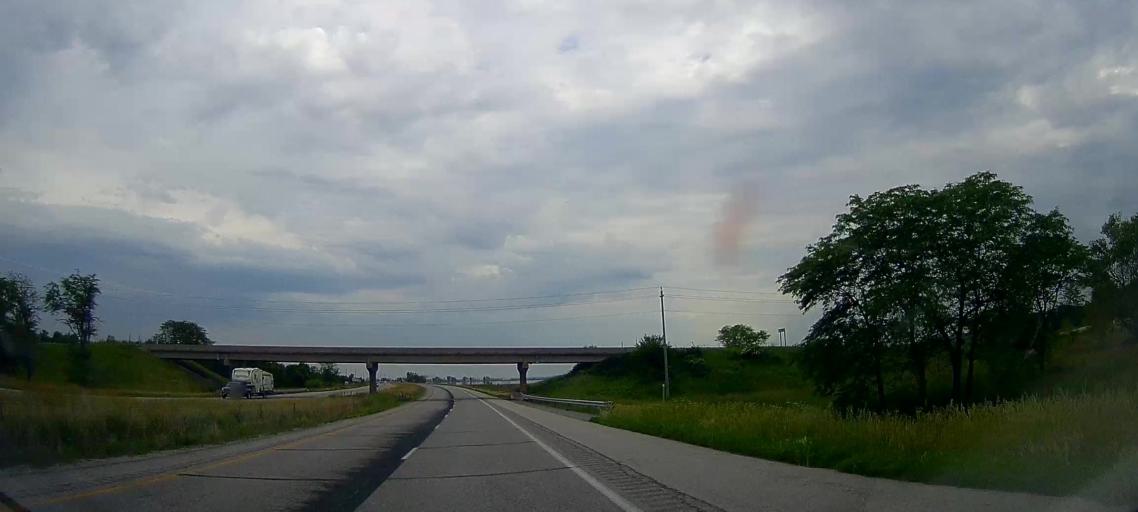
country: US
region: Iowa
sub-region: Pottawattamie County
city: Carter Lake
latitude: 41.4198
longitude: -95.9009
